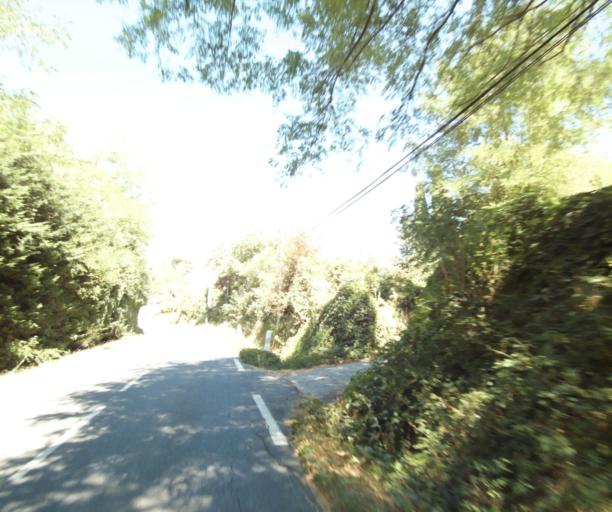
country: FR
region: Midi-Pyrenees
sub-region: Departement de la Haute-Garonne
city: Auzeville-Tolosane
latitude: 43.5150
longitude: 1.4798
